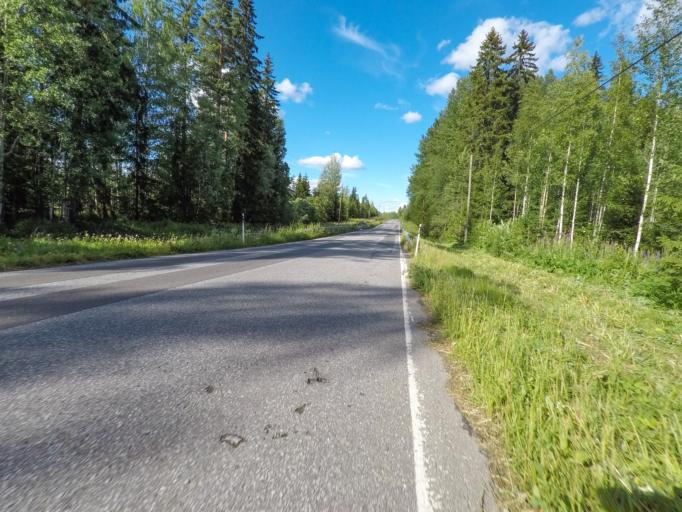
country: FI
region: South Karelia
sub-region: Imatra
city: Imatra
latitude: 61.1359
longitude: 28.7338
